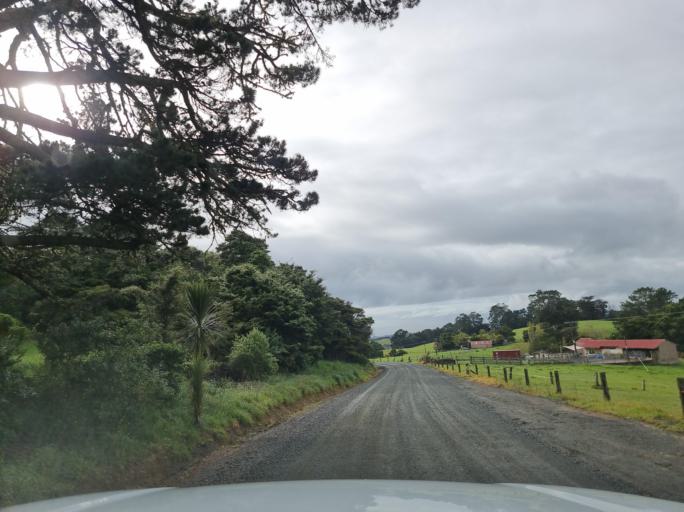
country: NZ
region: Northland
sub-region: Whangarei
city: Ruakaka
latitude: -35.9395
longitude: 174.3844
